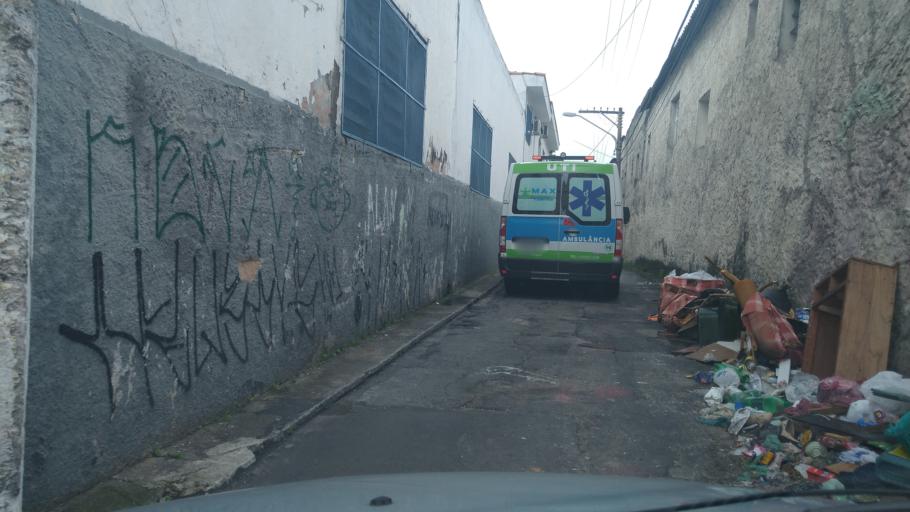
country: BR
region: Sao Paulo
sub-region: Sao Paulo
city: Sao Paulo
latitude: -23.5263
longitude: -46.6173
